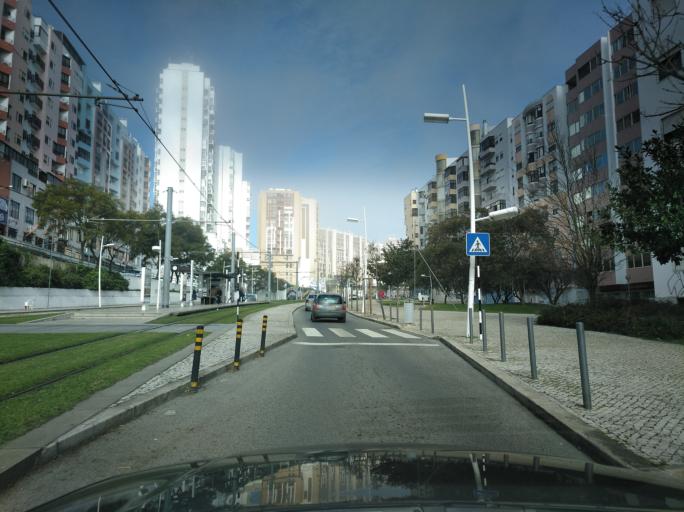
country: PT
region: Setubal
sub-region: Almada
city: Pragal
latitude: 38.6728
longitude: -9.1666
